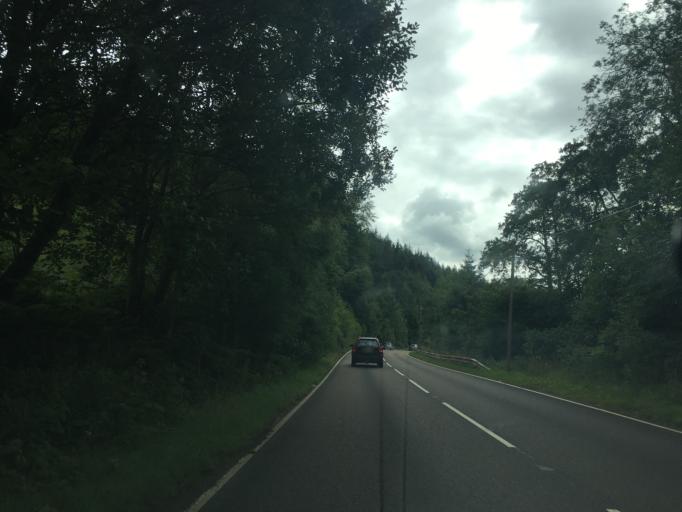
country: GB
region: Scotland
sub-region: Stirling
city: Callander
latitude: 56.2920
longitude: -4.2872
